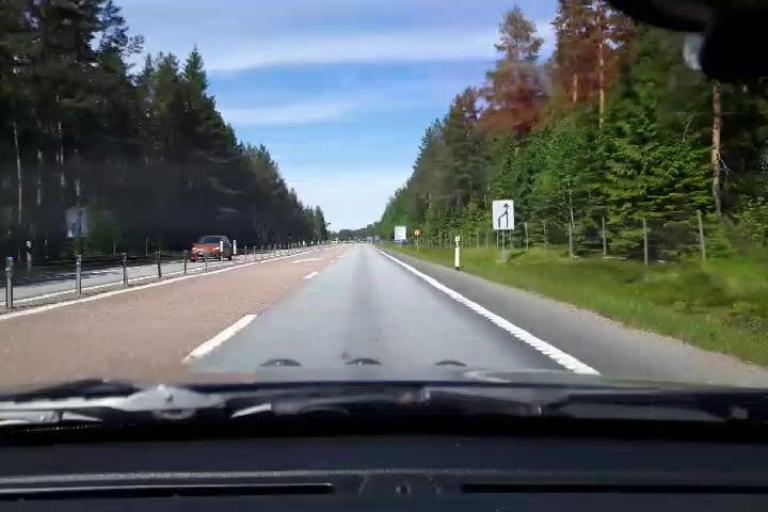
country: SE
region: Gaevleborg
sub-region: Gavle Kommun
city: Norrsundet
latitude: 61.0574
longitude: 16.9607
